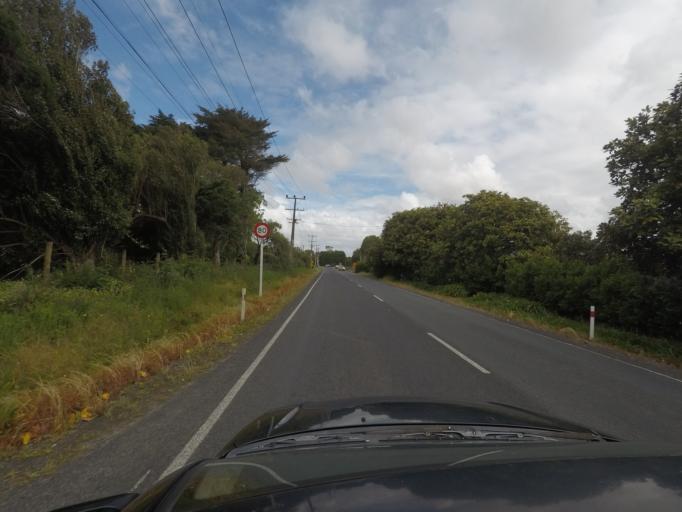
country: NZ
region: Auckland
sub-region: Auckland
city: Muriwai Beach
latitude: -36.7713
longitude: 174.5733
